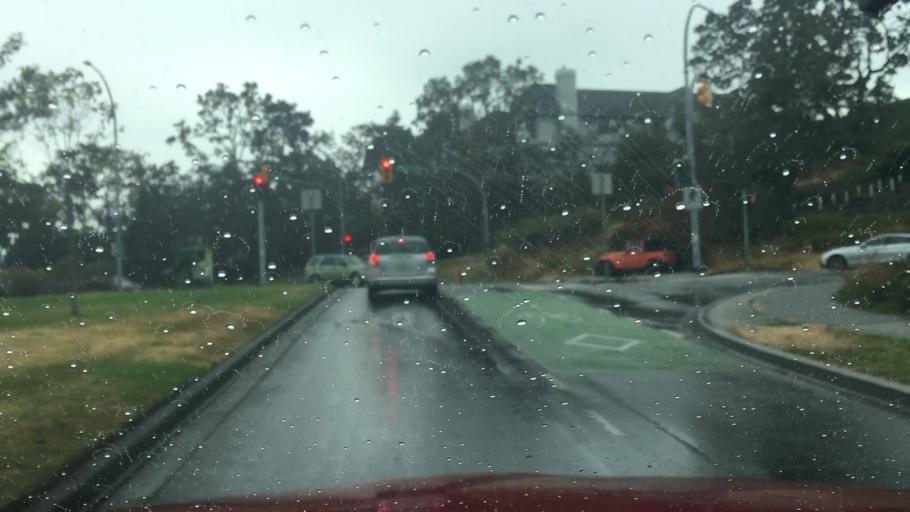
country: CA
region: British Columbia
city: Victoria
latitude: 48.4507
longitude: -123.3510
